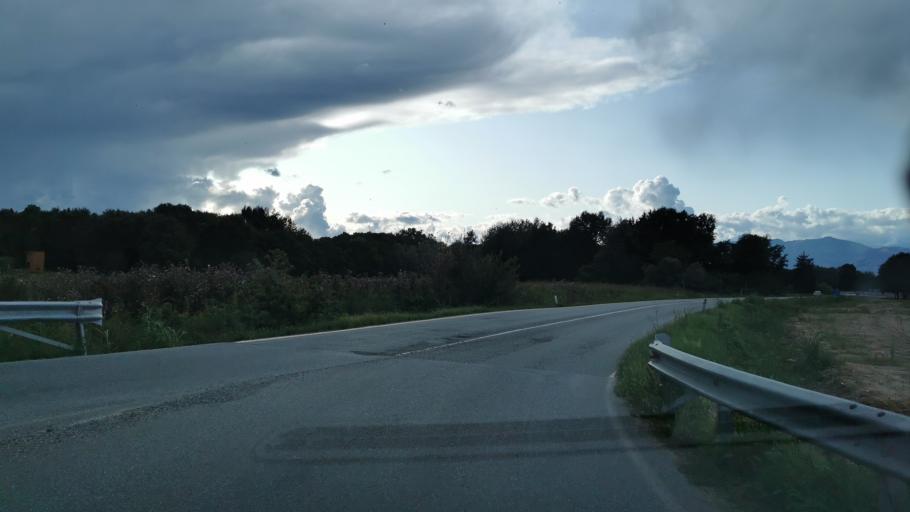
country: IT
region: Piedmont
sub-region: Provincia di Torino
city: Lombardore
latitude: 45.2287
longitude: 7.7546
